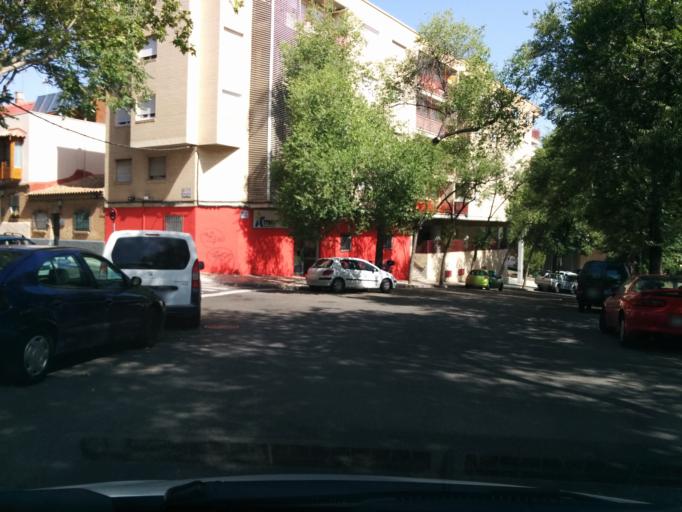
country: ES
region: Aragon
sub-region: Provincia de Zaragoza
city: Zaragoza
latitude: 41.6280
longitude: -0.8806
